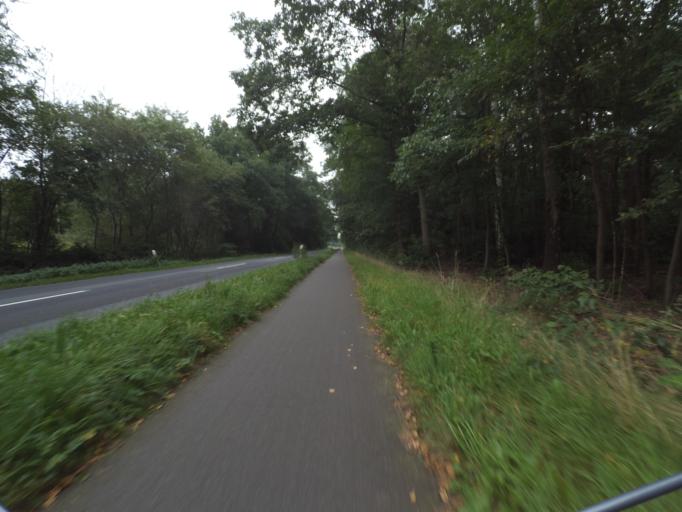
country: NL
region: Overijssel
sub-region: Gemeente Losser
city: Losser
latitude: 52.2807
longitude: 7.0790
